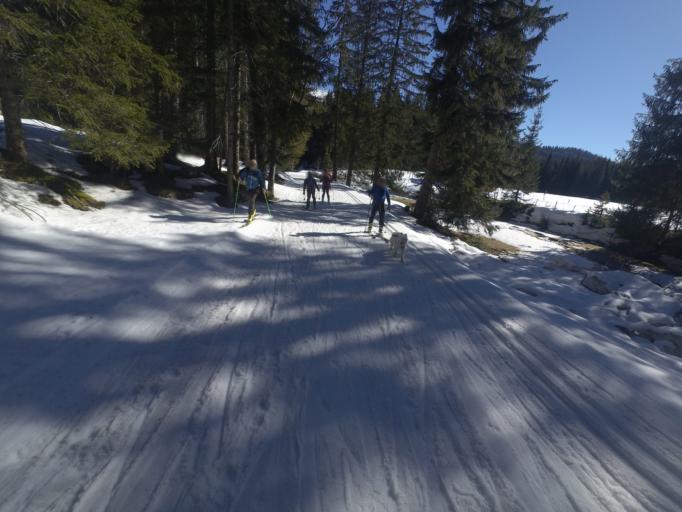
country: AT
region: Salzburg
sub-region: Politischer Bezirk Salzburg-Umgebung
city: Strobl
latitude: 47.6484
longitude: 13.4183
